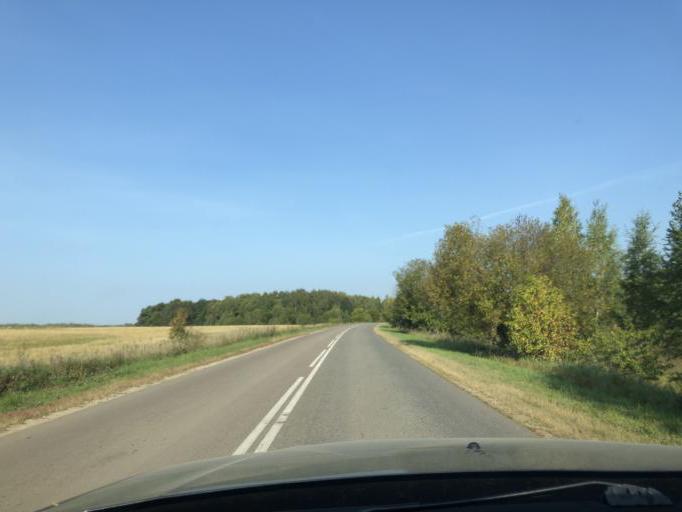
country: RU
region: Tula
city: Novogurovskiy
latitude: 54.3641
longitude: 37.3378
